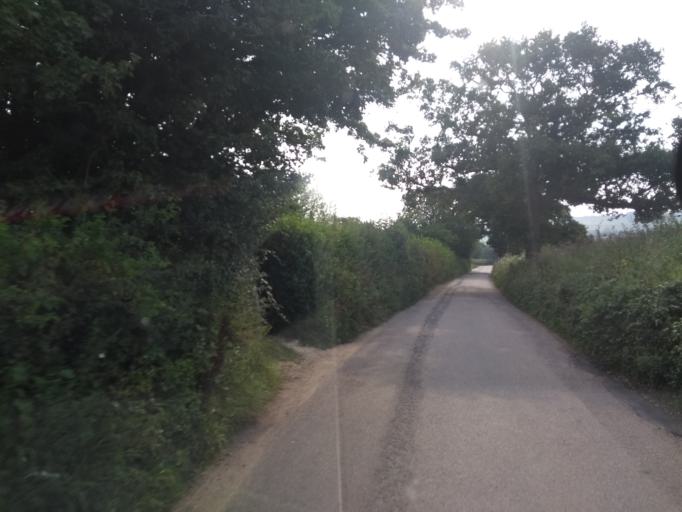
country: GB
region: England
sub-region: Devon
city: Colyton
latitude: 50.7523
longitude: -3.0444
